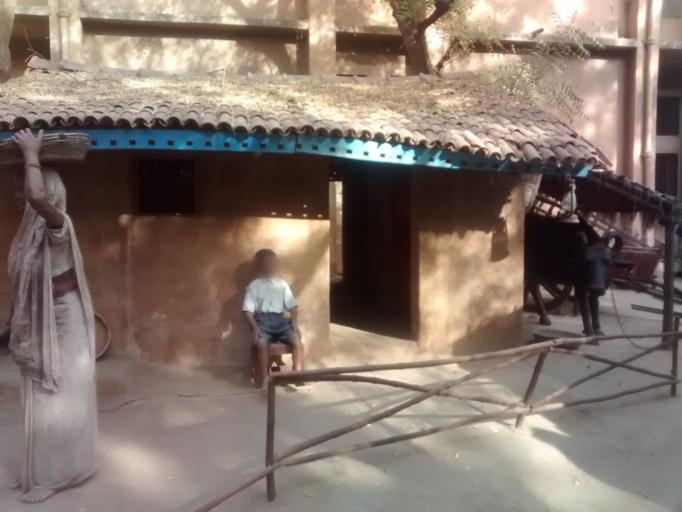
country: IN
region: Gujarat
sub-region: Ahmadabad
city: Ahmedabad
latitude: 23.0448
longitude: 72.5696
